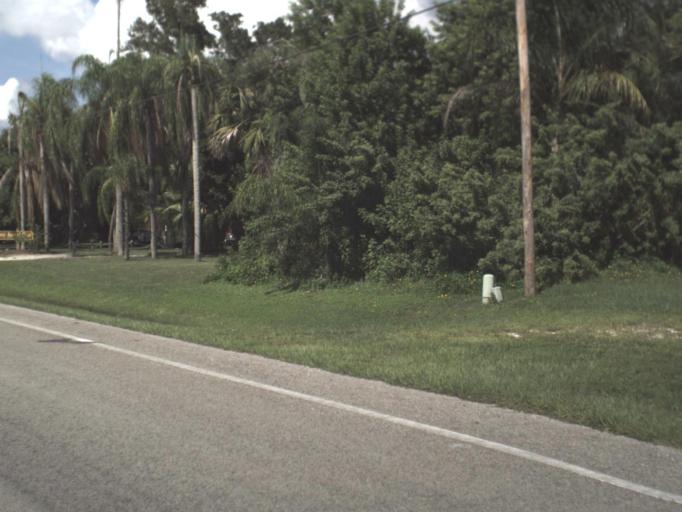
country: US
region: Florida
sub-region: Sarasota County
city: Osprey
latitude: 27.1887
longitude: -82.4867
